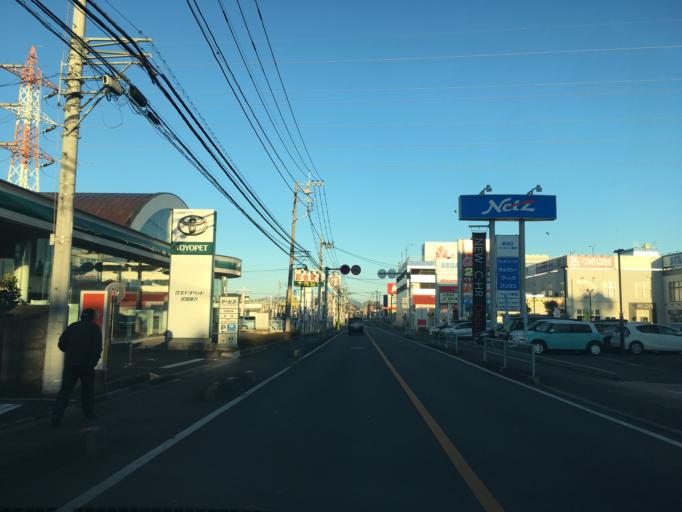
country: JP
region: Saitama
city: Sayama
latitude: 35.8182
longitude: 139.4185
